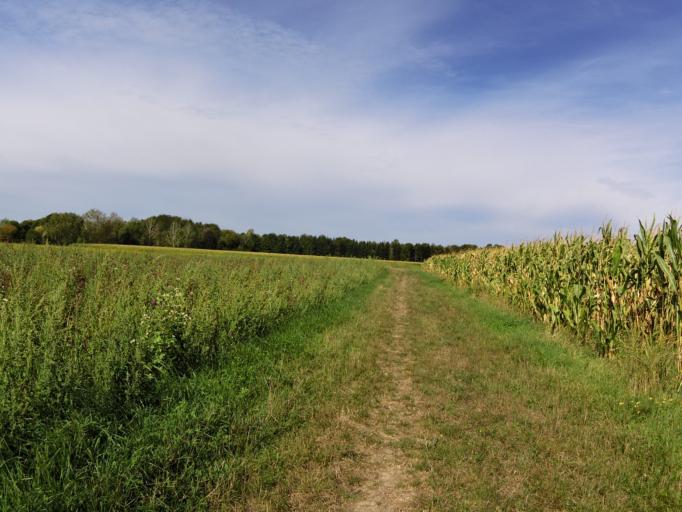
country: DE
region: Baden-Wuerttemberg
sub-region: Freiburg Region
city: Lahr
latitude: 48.3548
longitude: 7.8416
